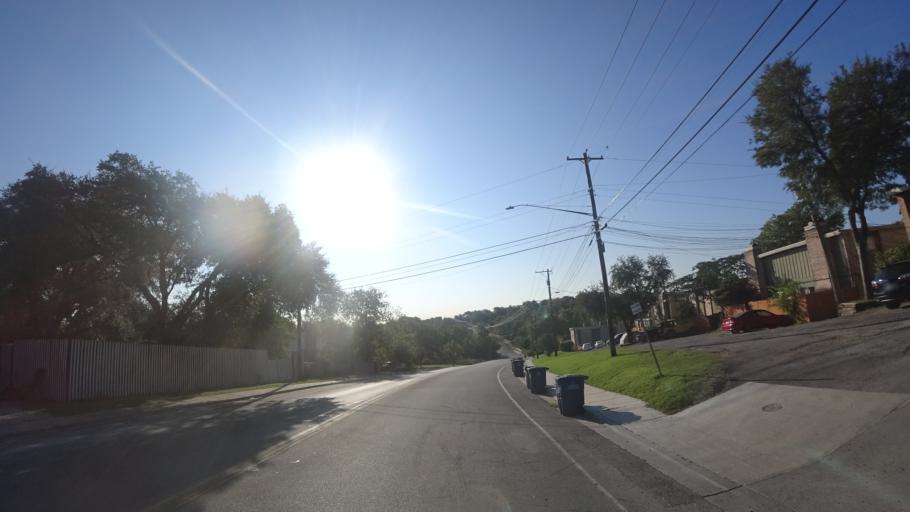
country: US
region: Texas
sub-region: Travis County
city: Austin
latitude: 30.3131
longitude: -97.6778
